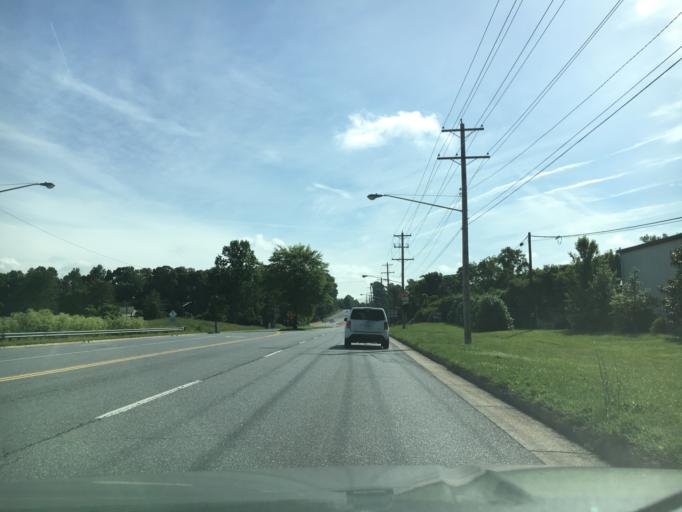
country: US
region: Virginia
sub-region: City of Lynchburg
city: West Lynchburg
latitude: 37.3760
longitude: -79.2234
